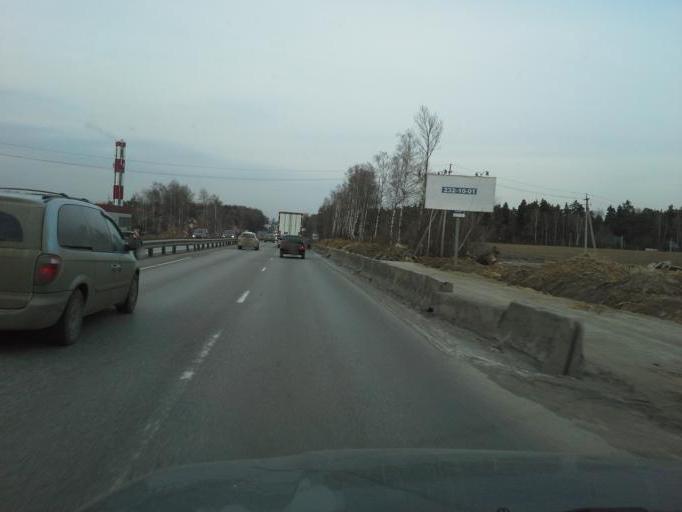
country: RU
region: Moskovskaya
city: Odintsovo
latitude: 55.6622
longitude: 37.3034
